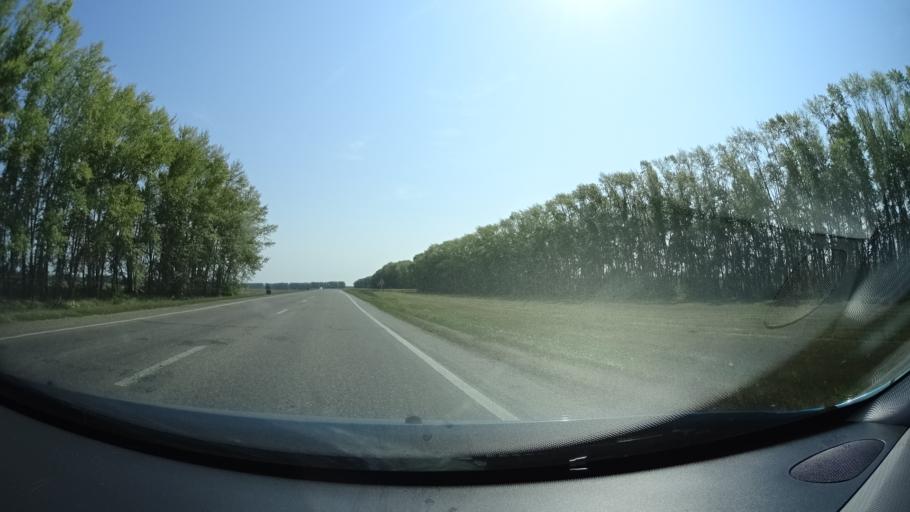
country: RU
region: Bashkortostan
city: Karmaskaly
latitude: 54.3904
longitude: 56.1239
